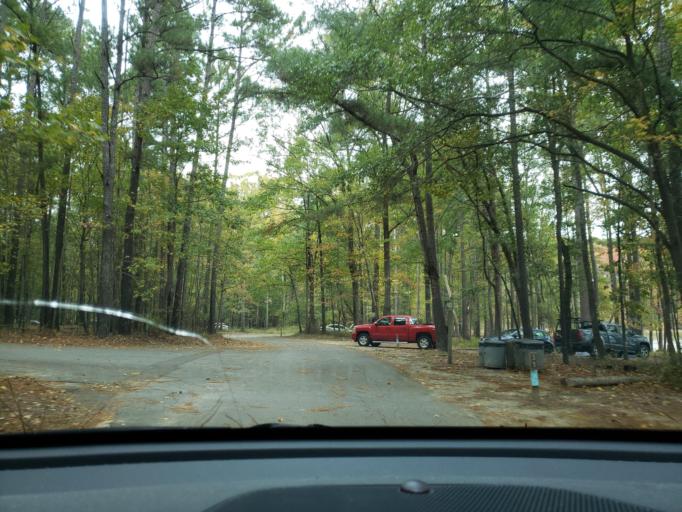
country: US
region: North Carolina
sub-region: Chatham County
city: Fearrington Village
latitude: 35.7430
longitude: -79.0342
